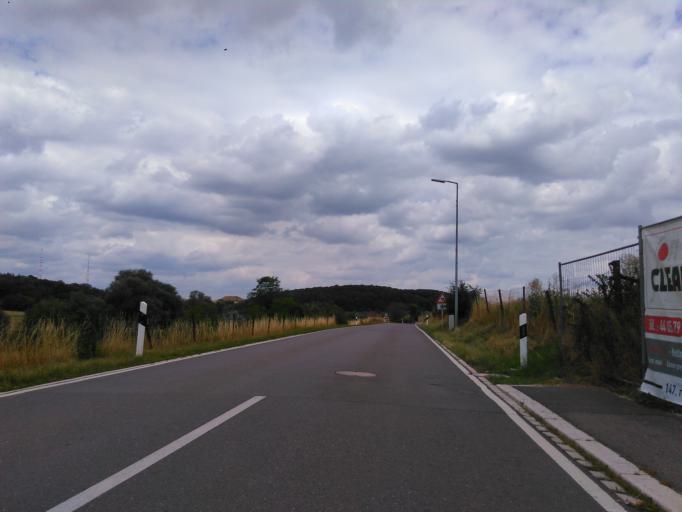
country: LU
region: Grevenmacher
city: Gonderange
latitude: 49.6942
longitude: 6.2560
